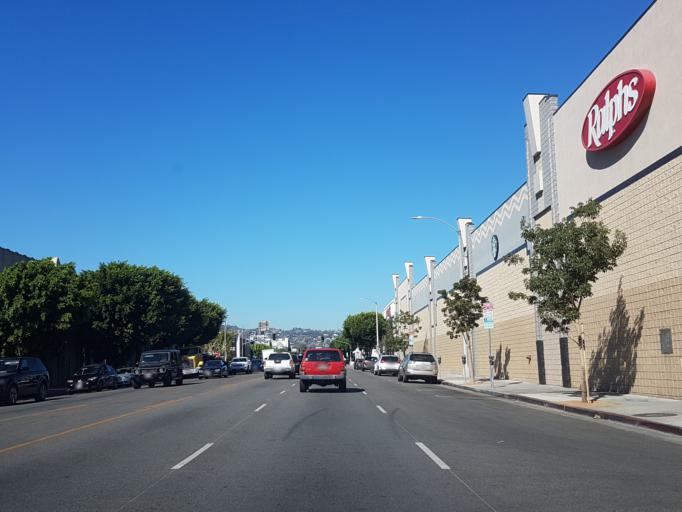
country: US
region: California
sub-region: Los Angeles County
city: West Hollywood
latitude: 34.0696
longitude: -118.3440
